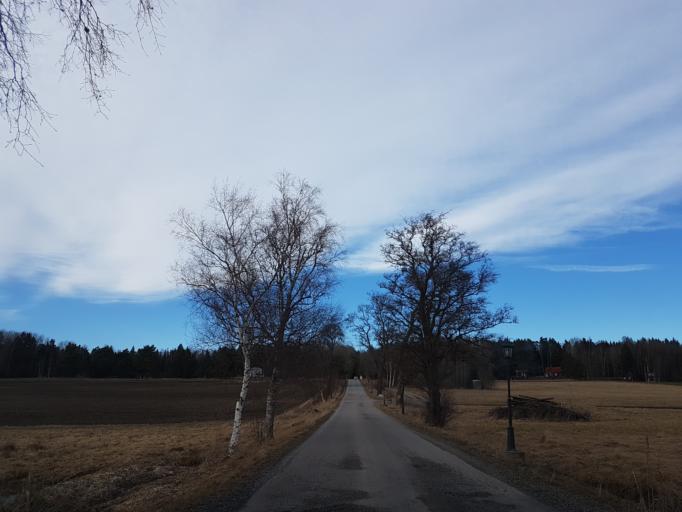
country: SE
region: Stockholm
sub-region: Norrtalje Kommun
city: Nykvarn
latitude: 59.7377
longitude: 18.1910
